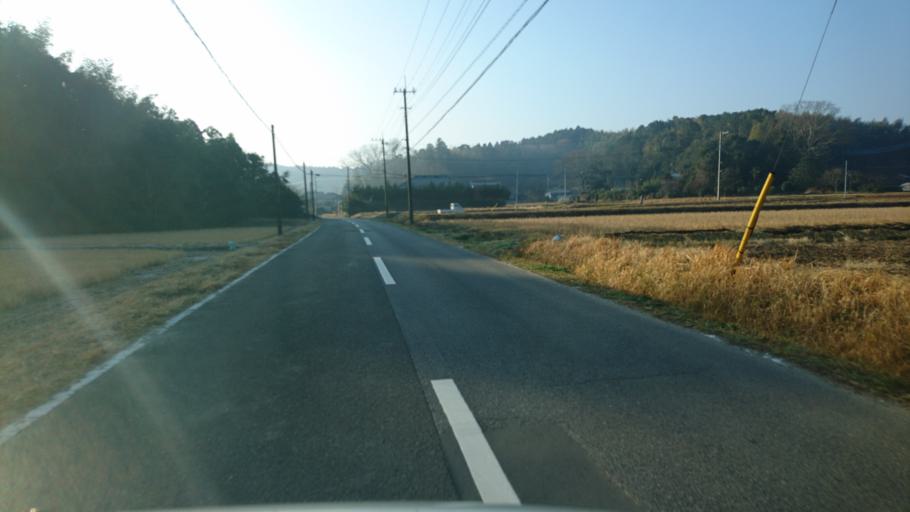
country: JP
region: Chiba
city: Kimitsu
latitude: 35.2994
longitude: 139.9481
